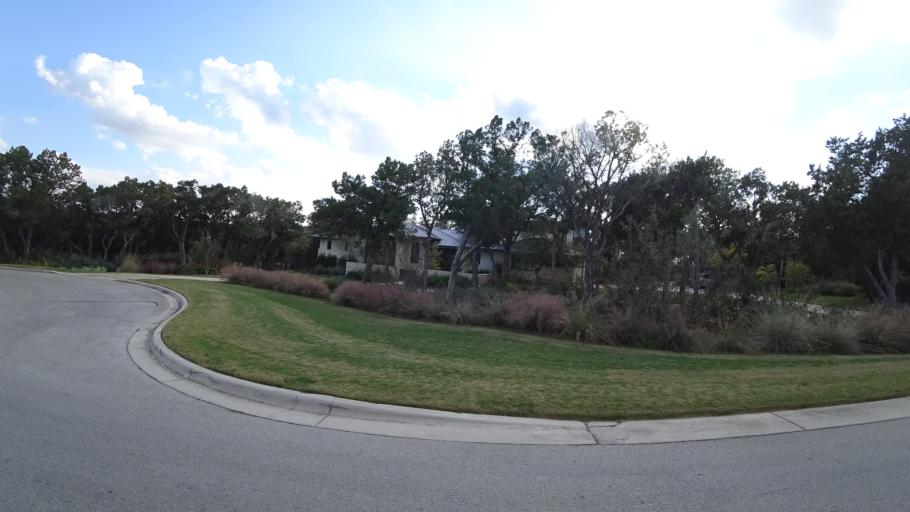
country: US
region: Texas
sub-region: Travis County
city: Barton Creek
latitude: 30.2768
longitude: -97.8798
